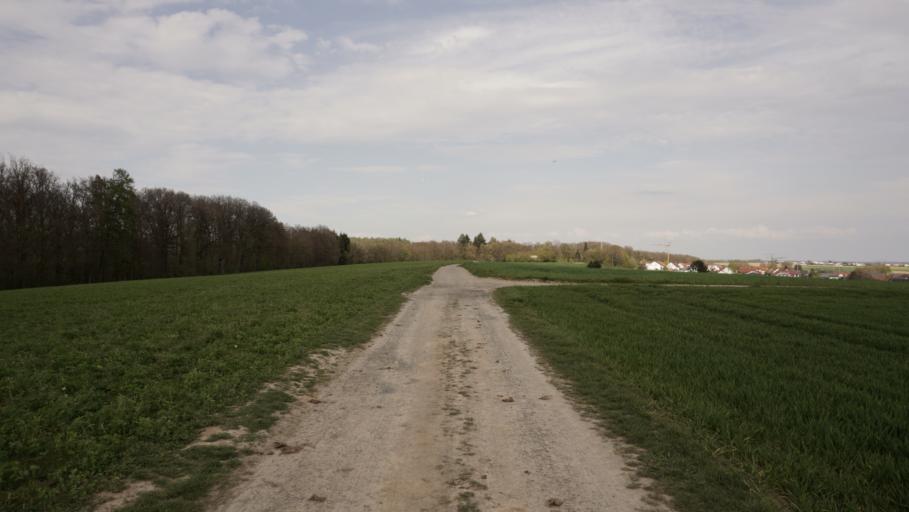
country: DE
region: Baden-Wuerttemberg
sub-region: Karlsruhe Region
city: Neckargerach
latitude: 49.3995
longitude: 9.0898
